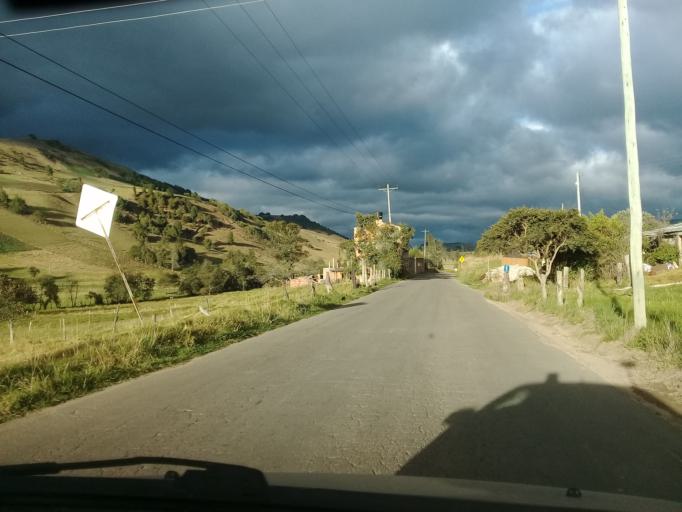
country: CO
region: Cundinamarca
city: Villapinzon
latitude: 5.2195
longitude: -73.6182
